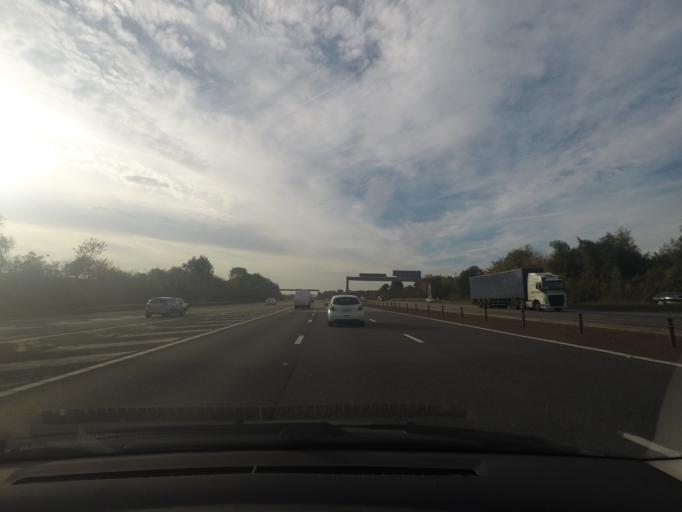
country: GB
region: England
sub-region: City and Borough of Leeds
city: Swillington
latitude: 53.7883
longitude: -1.4277
